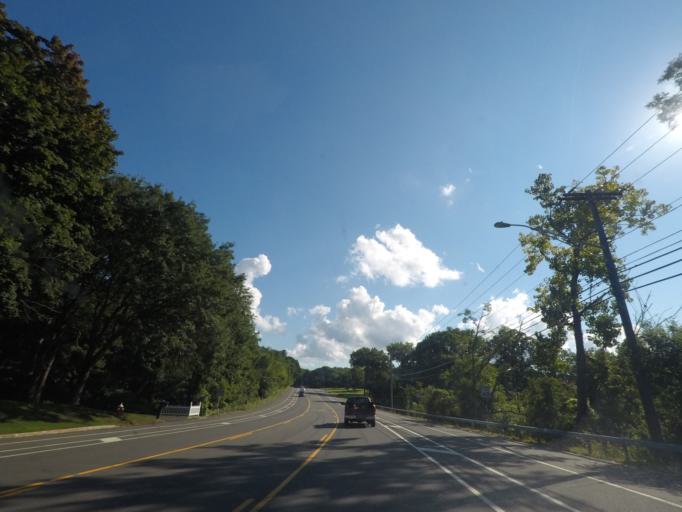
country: US
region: New York
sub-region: Albany County
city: Menands
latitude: 42.6976
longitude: -73.7394
